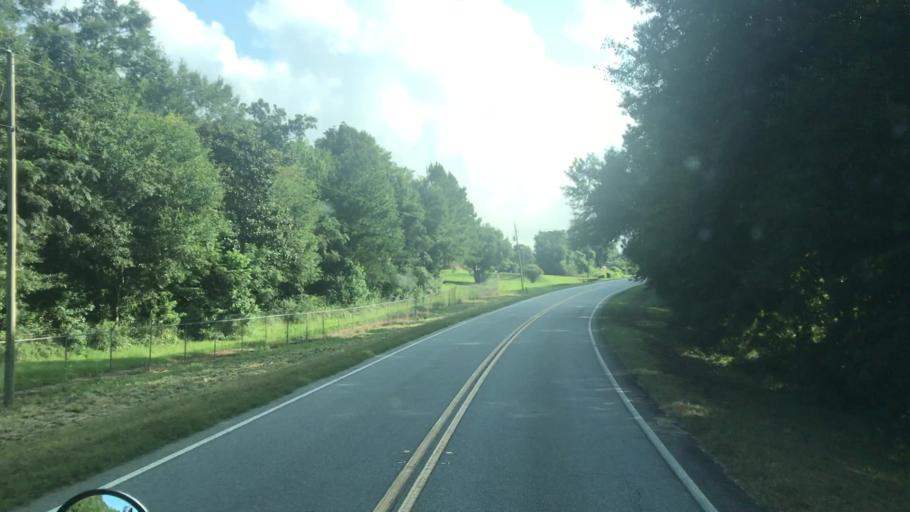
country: US
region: Florida
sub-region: Gadsden County
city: Havana
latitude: 30.7317
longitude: -84.4853
